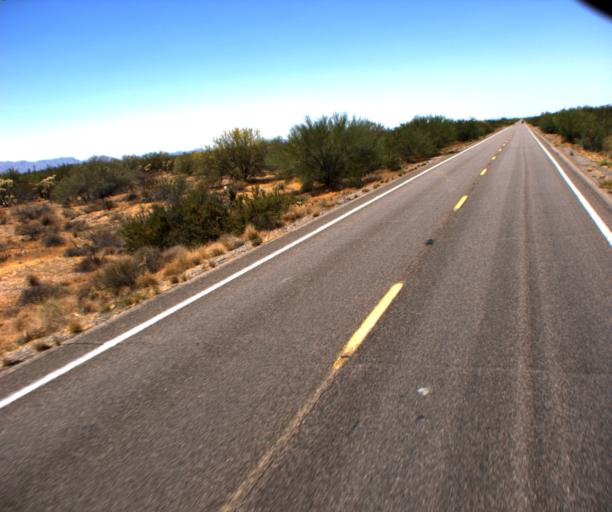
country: US
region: Arizona
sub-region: Pima County
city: Catalina
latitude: 32.7516
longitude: -111.1347
